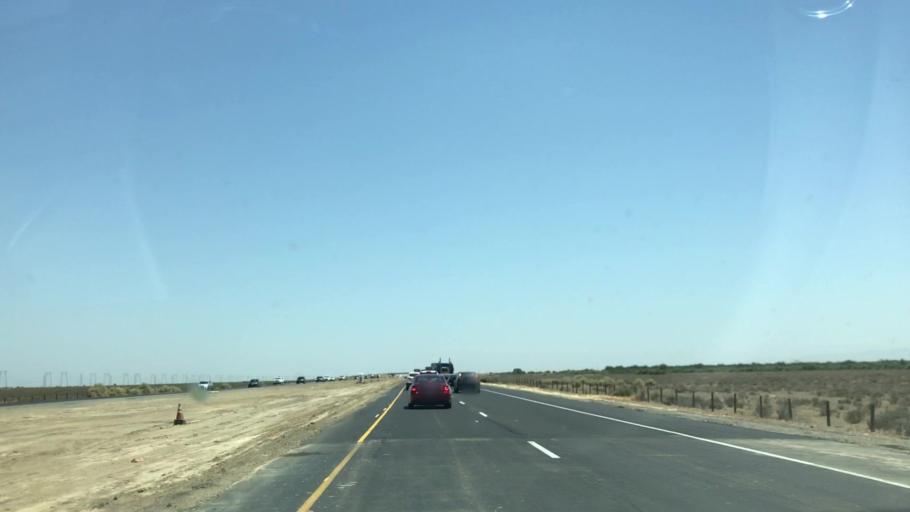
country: US
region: California
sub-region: Kern County
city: Lost Hills
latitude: 35.8036
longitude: -119.7930
